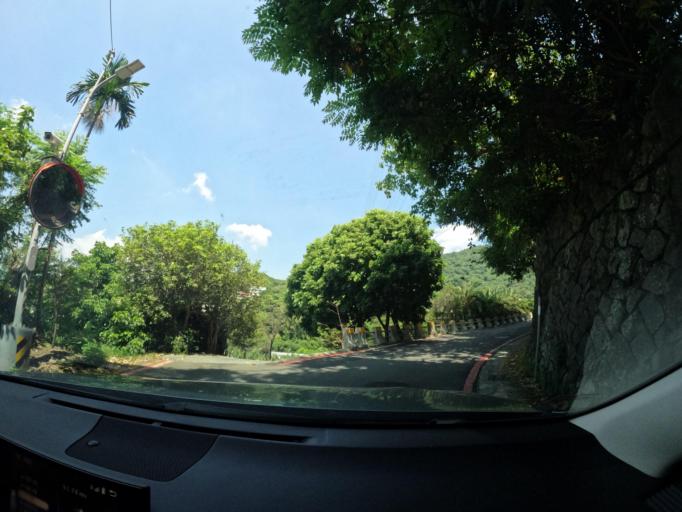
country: TW
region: Taipei
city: Taipei
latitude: 25.1175
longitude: 121.5396
